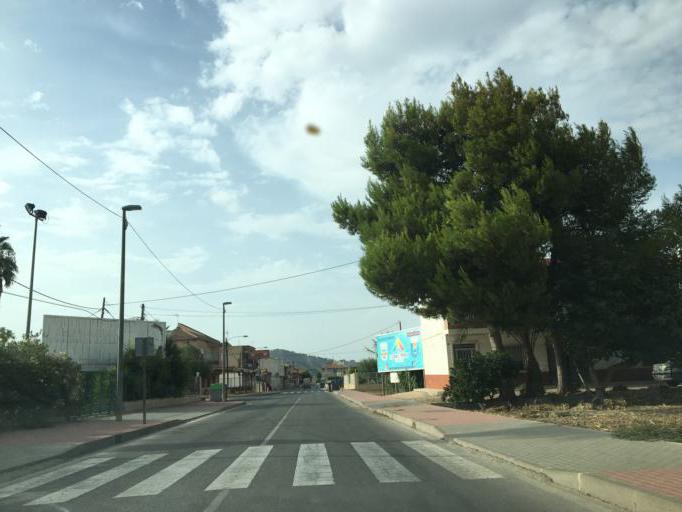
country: ES
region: Murcia
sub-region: Murcia
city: Murcia
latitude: 38.0113
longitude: -1.0812
